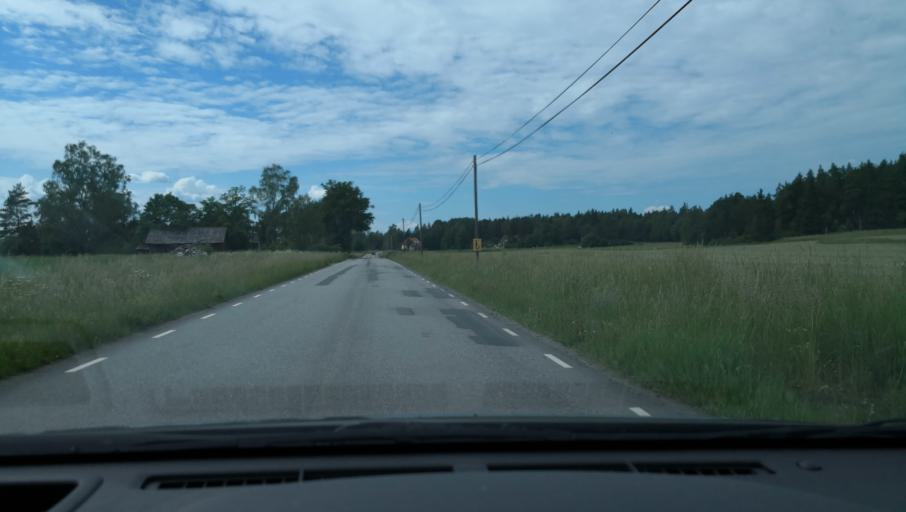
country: SE
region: Uppsala
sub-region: Uppsala Kommun
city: Uppsala
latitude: 59.8073
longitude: 17.5264
